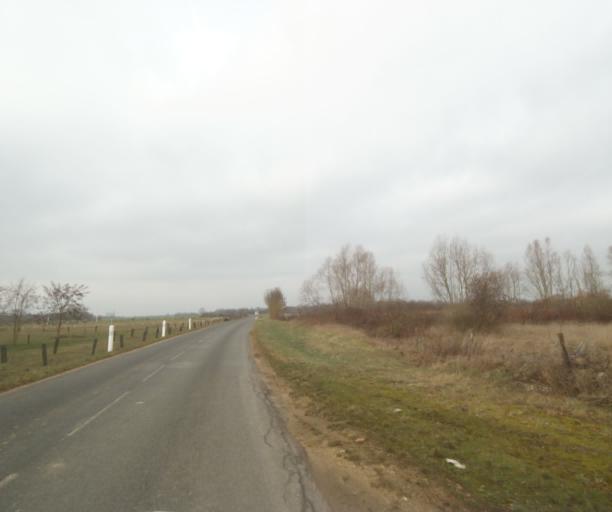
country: FR
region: Champagne-Ardenne
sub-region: Departement de la Haute-Marne
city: Villiers-en-Lieu
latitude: 48.6513
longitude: 4.8064
